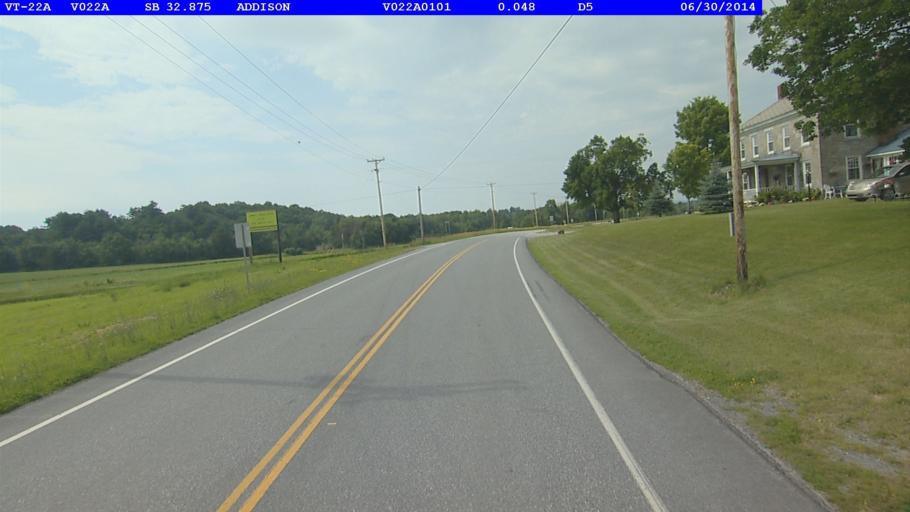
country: US
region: Vermont
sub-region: Addison County
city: Middlebury (village)
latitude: 44.0306
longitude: -73.3076
